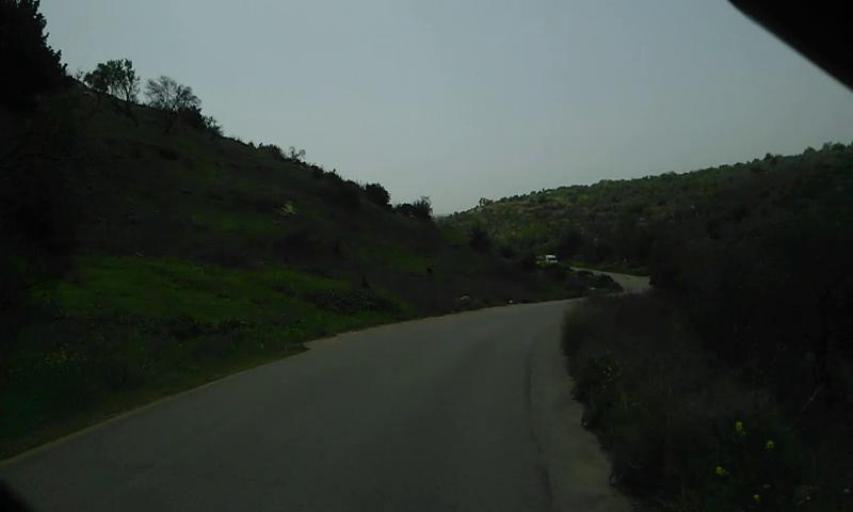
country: PS
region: West Bank
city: Silat al Harithiyah
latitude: 32.5127
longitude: 35.2136
